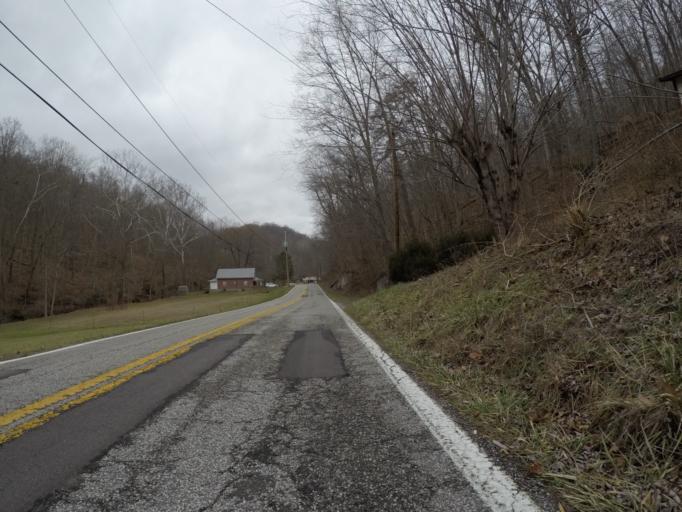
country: US
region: West Virginia
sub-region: Cabell County
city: Barboursville
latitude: 38.4464
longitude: -82.2532
